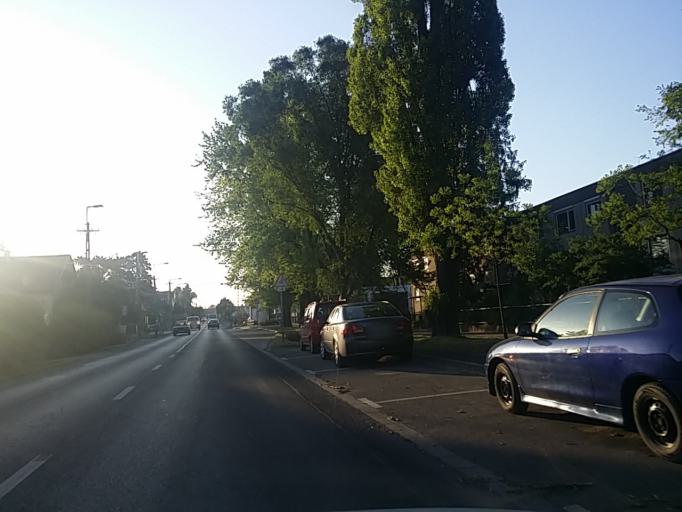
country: HU
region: Pest
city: Dunakeszi
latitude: 47.6272
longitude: 19.1498
